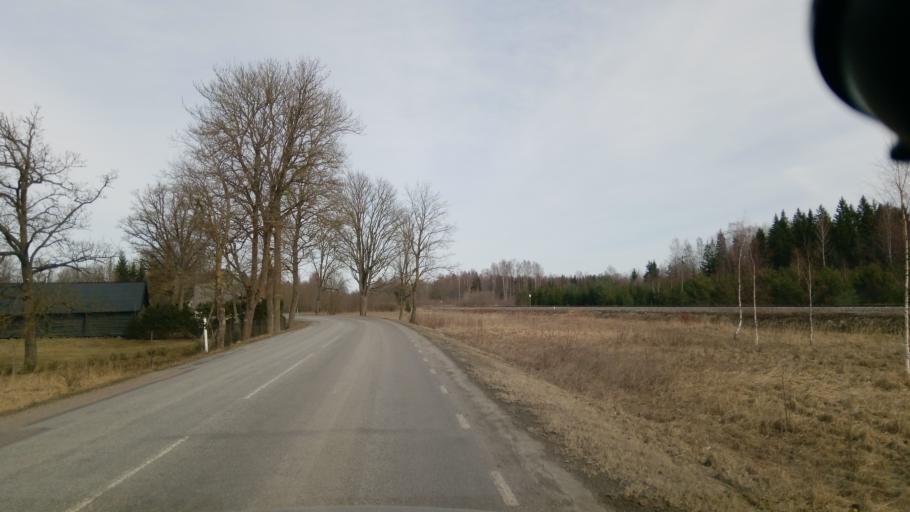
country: EE
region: Raplamaa
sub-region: Rapla vald
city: Rapla
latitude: 59.0207
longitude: 24.8378
